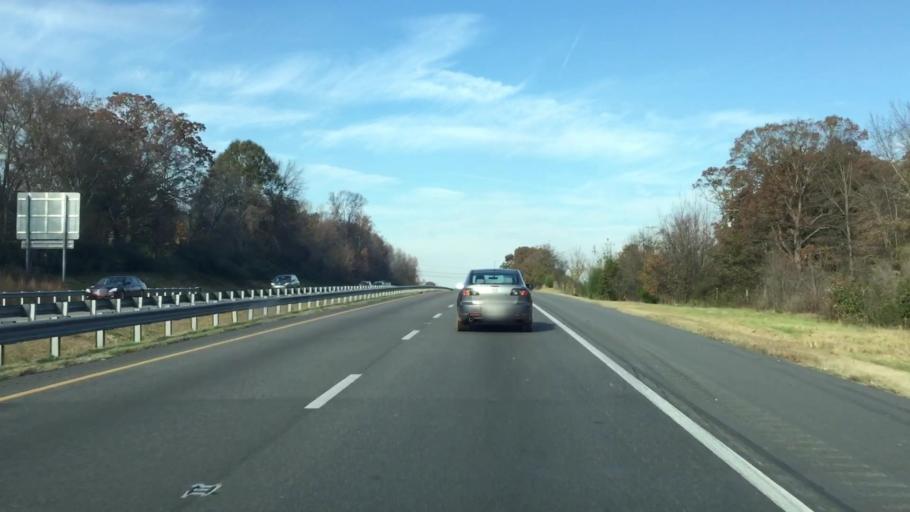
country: US
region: North Carolina
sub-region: Iredell County
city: Statesville
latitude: 35.7985
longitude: -80.8618
